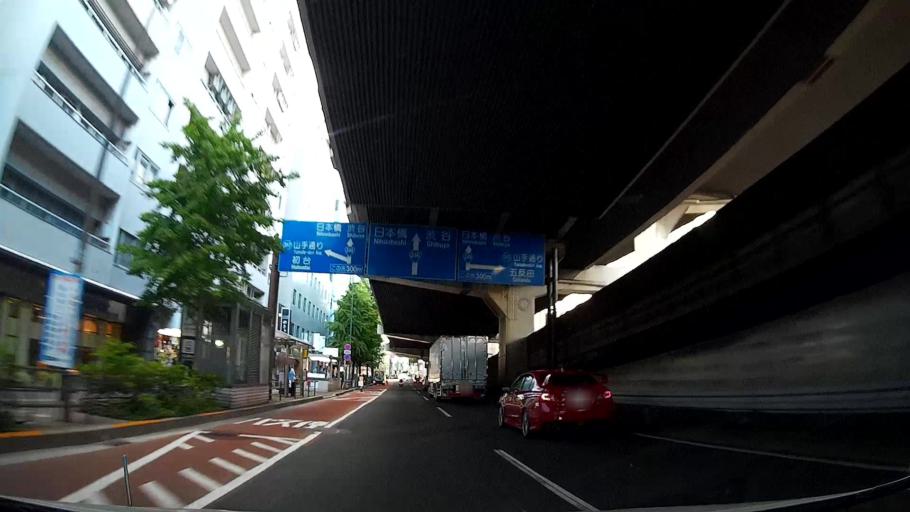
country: JP
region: Tokyo
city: Tokyo
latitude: 35.6507
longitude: 139.6840
